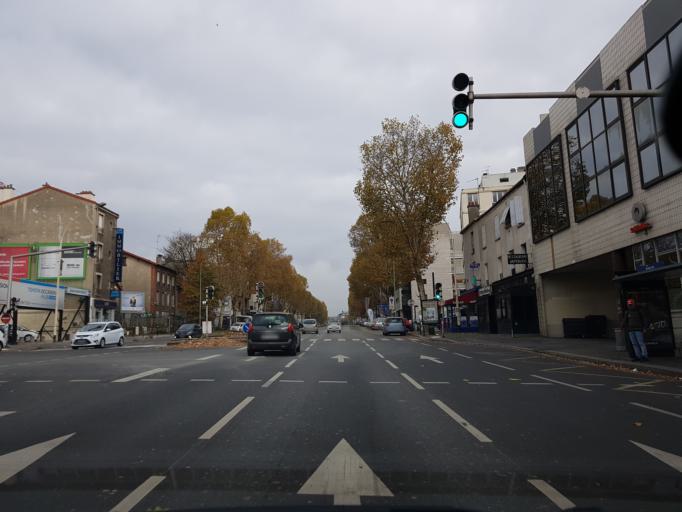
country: FR
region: Ile-de-France
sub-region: Departement du Val-de-Marne
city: Arcueil
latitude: 48.8016
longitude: 2.3241
